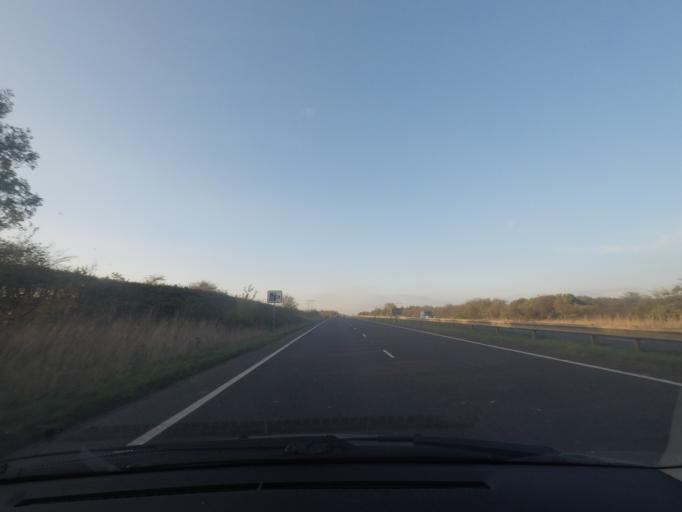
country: GB
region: England
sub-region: North Lincolnshire
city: Barnetby le Wold
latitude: 53.5950
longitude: -0.4189
